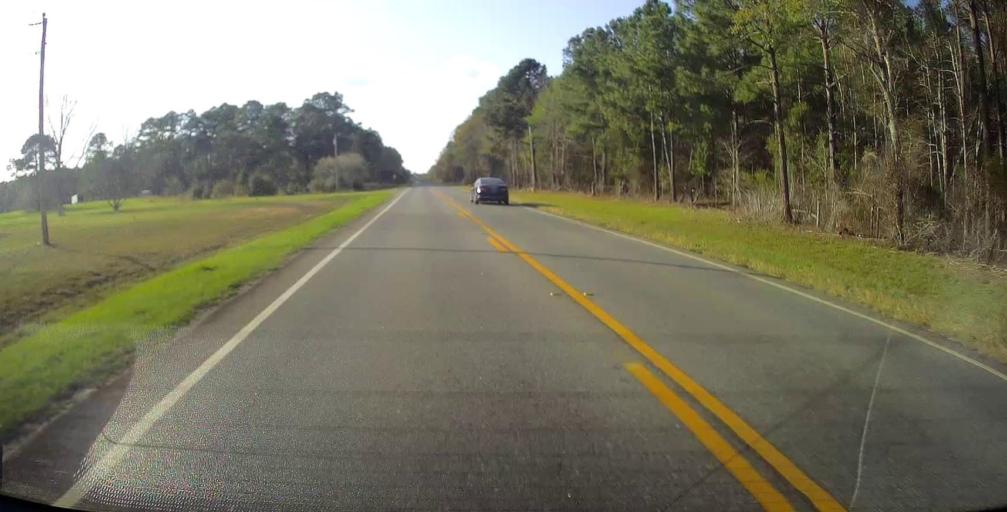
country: US
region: Georgia
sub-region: Toombs County
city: Lyons
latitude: 32.1785
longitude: -82.2884
